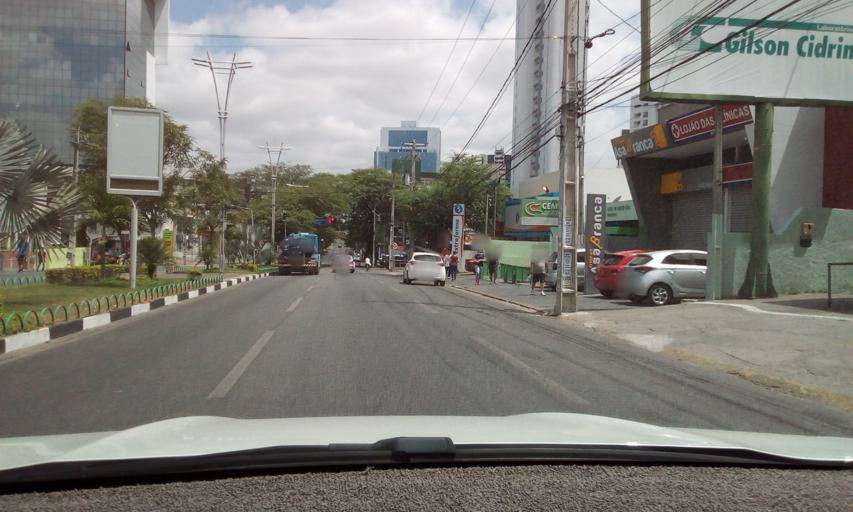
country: BR
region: Pernambuco
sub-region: Caruaru
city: Caruaru
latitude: -8.2746
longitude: -35.9738
